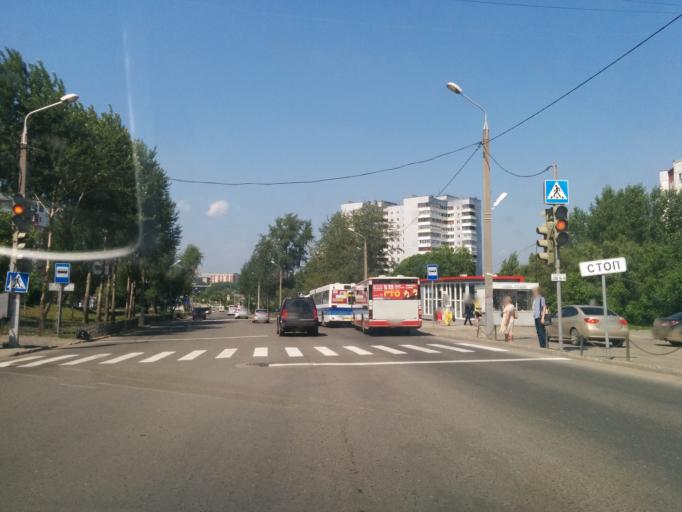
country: RU
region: Perm
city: Perm
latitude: 58.0087
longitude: 56.3090
